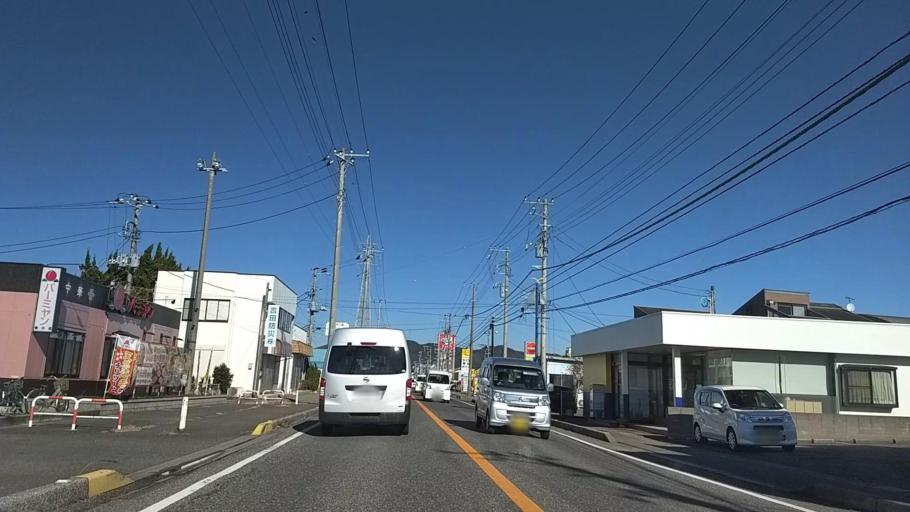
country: JP
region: Chiba
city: Kawaguchi
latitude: 35.1026
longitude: 140.0950
